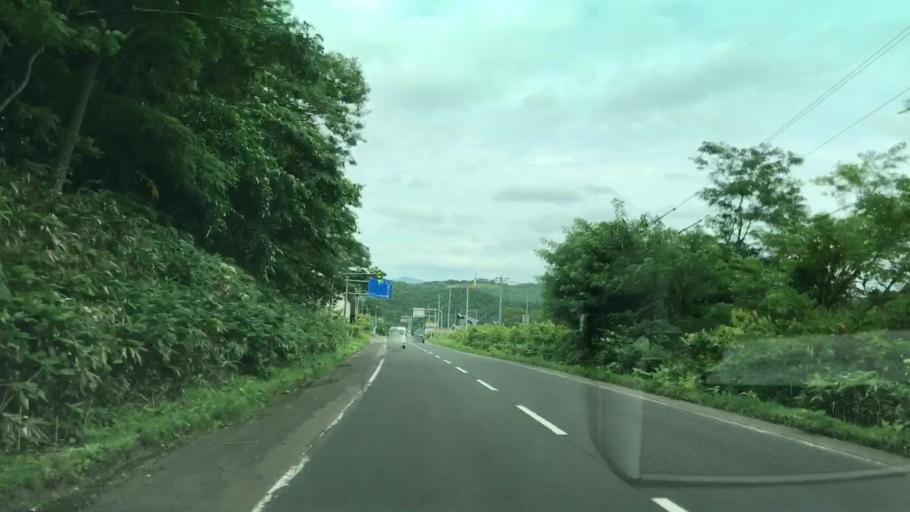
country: JP
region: Hokkaido
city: Niseko Town
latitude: 42.9567
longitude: 140.6960
